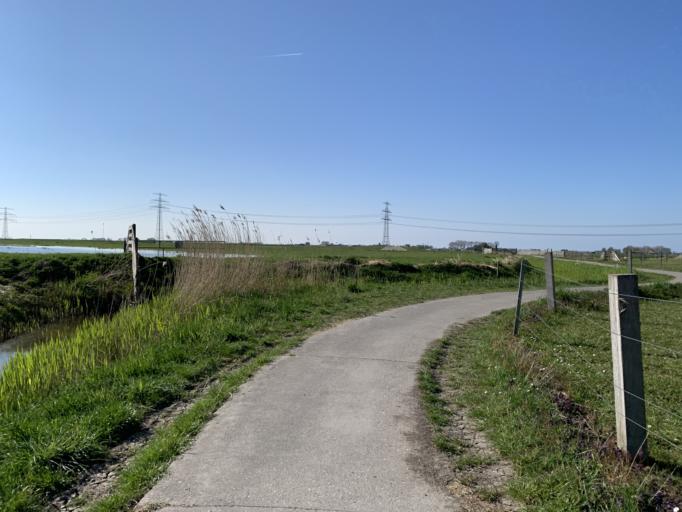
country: NL
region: Groningen
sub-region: Gemeente Winsum
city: Winsum
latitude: 53.2885
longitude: 6.5139
